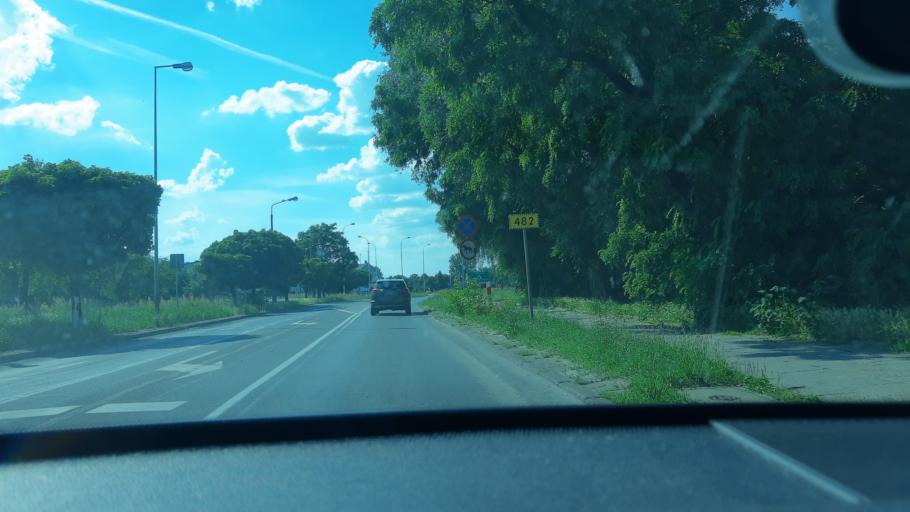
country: PL
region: Lodz Voivodeship
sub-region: Powiat zdunskowolski
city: Zdunska Wola
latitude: 51.6054
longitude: 18.9410
